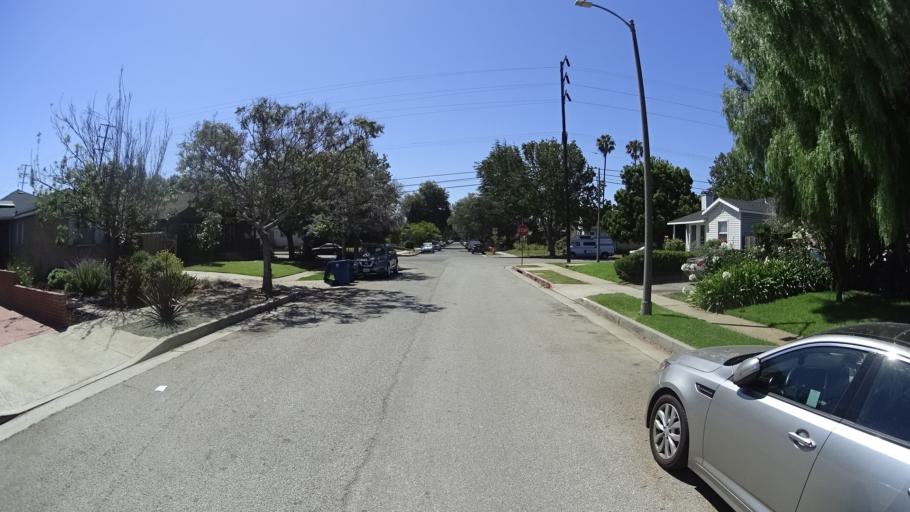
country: US
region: California
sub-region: Los Angeles County
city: Westwood, Los Angeles
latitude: 34.0265
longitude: -118.4504
